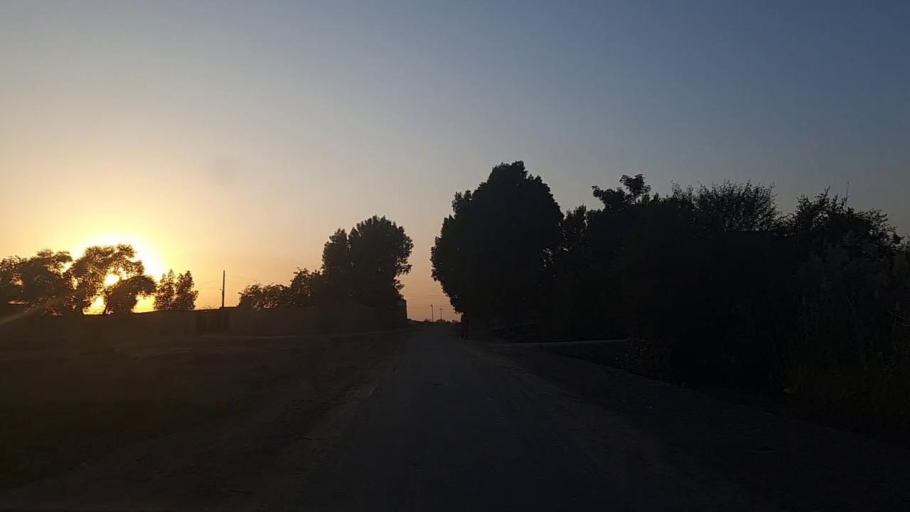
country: PK
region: Sindh
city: Jam Sahib
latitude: 26.3673
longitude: 68.7105
